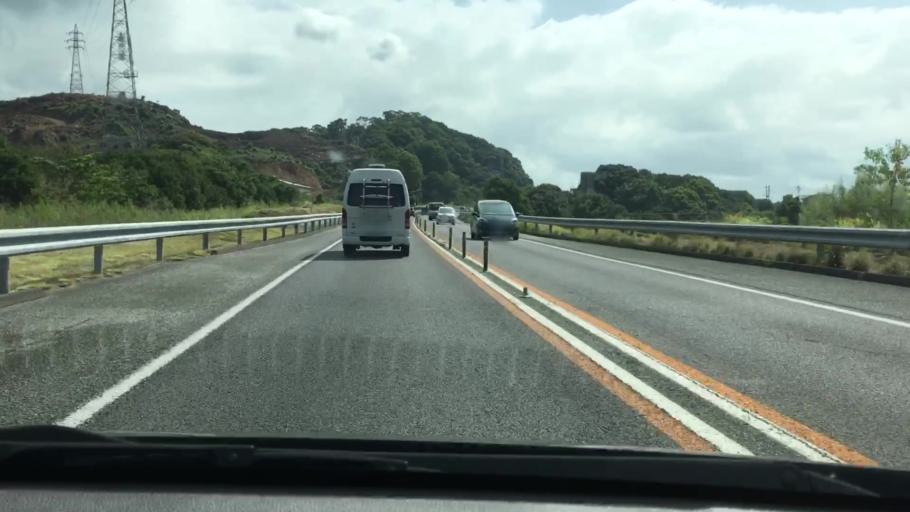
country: JP
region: Nagasaki
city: Sasebo
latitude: 33.1516
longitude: 129.7593
